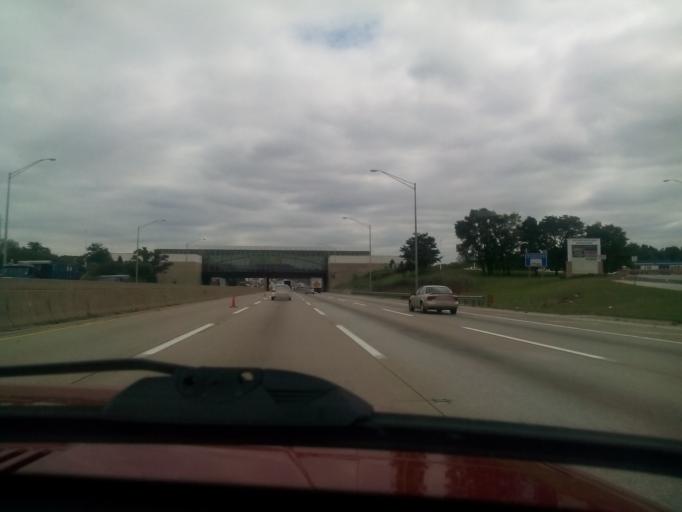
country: US
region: Illinois
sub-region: Cook County
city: Thornton
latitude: 41.5791
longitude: -87.6022
